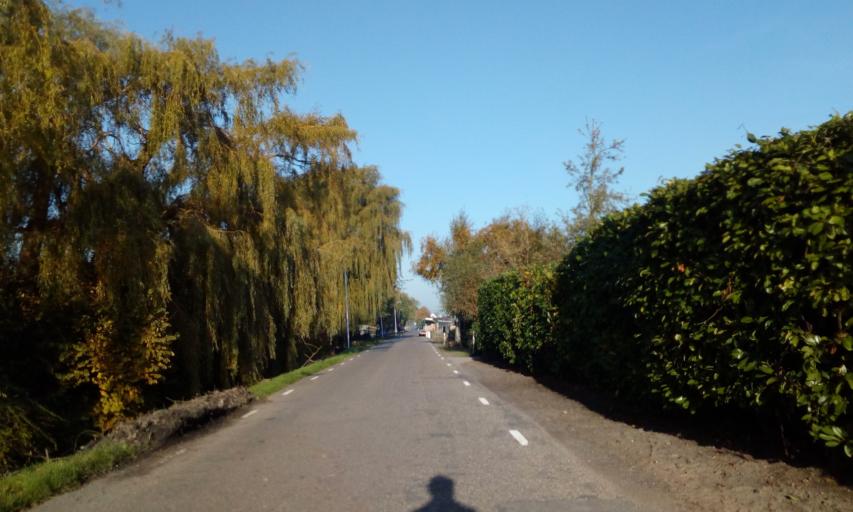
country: NL
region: South Holland
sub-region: Gemeente Lansingerland
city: Berkel en Rodenrijs
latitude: 51.9739
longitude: 4.4368
